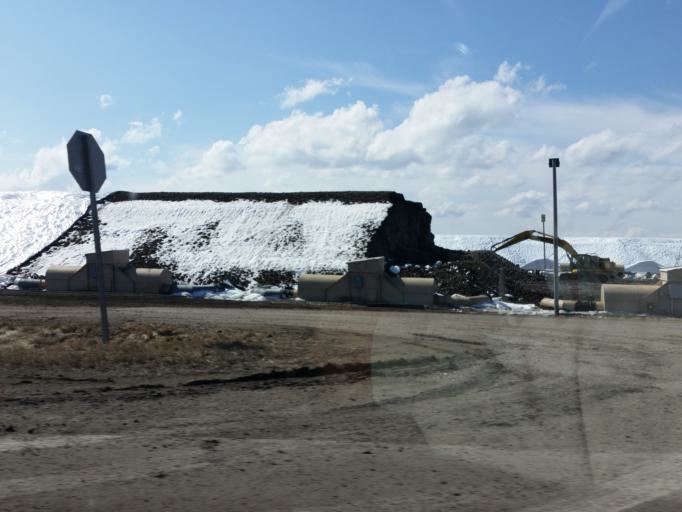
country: US
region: North Dakota
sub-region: Walsh County
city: Grafton
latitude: 48.2143
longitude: -97.3624
